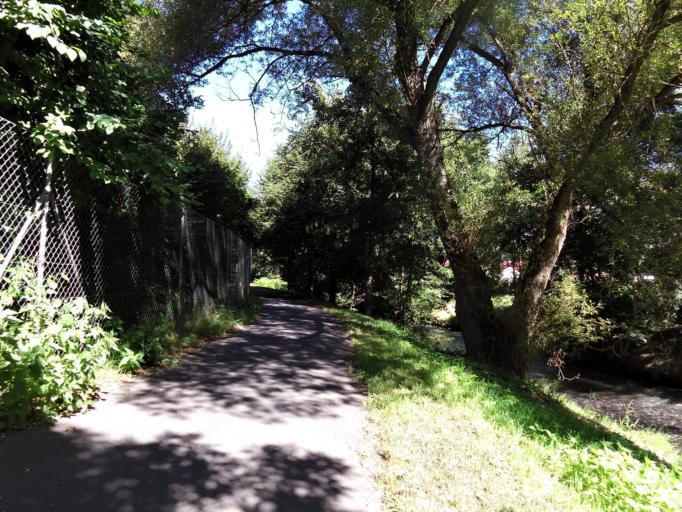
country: DE
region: Hesse
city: Michelstadt
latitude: 49.6738
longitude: 8.9962
